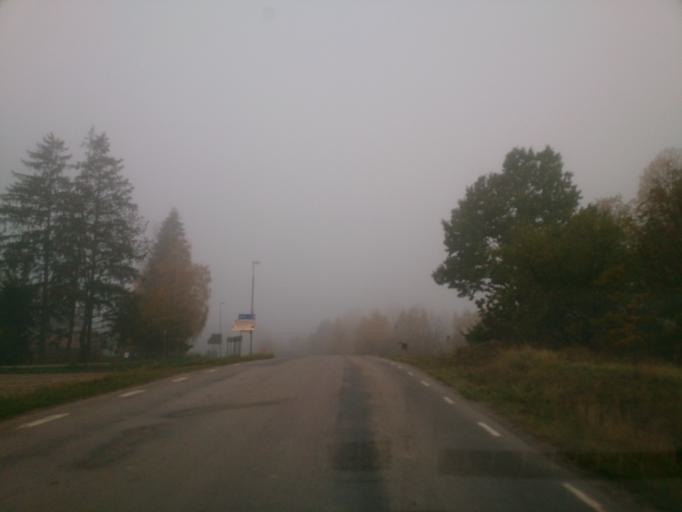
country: SE
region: OEstergoetland
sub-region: Kinda Kommun
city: Rimforsa
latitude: 58.1410
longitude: 15.6996
